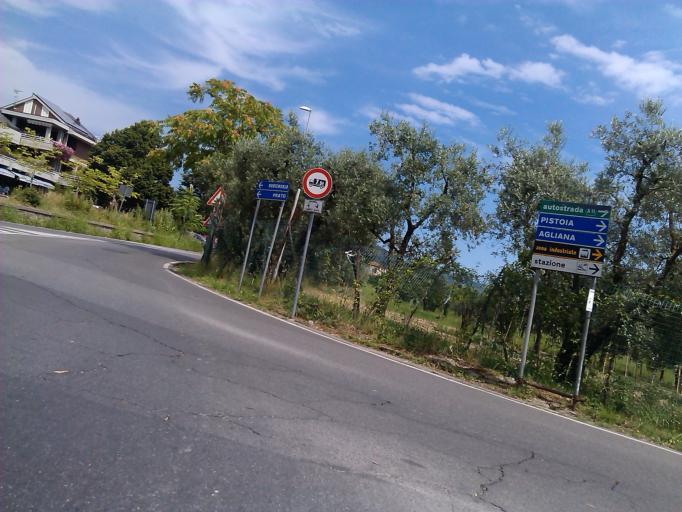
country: IT
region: Tuscany
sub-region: Provincia di Pistoia
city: Montale
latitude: 43.9315
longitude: 11.0238
